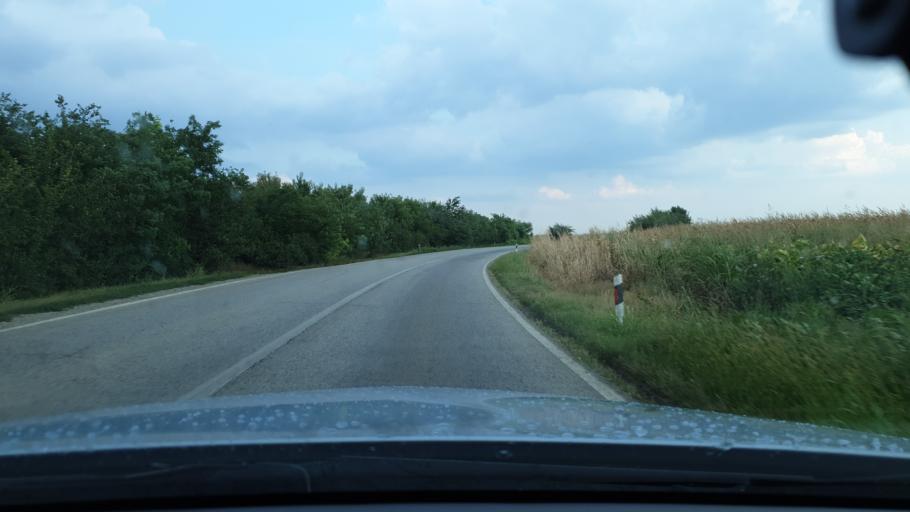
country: RS
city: Sutjeska
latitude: 45.3820
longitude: 20.7255
